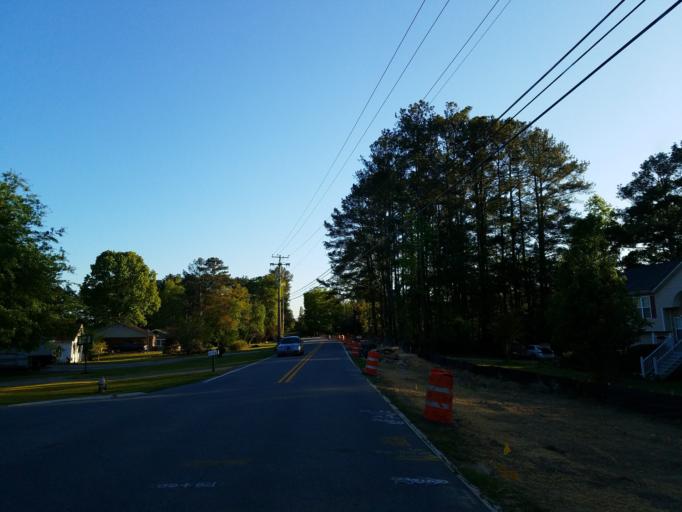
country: US
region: Georgia
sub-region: Cobb County
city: Powder Springs
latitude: 33.9148
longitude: -84.6356
